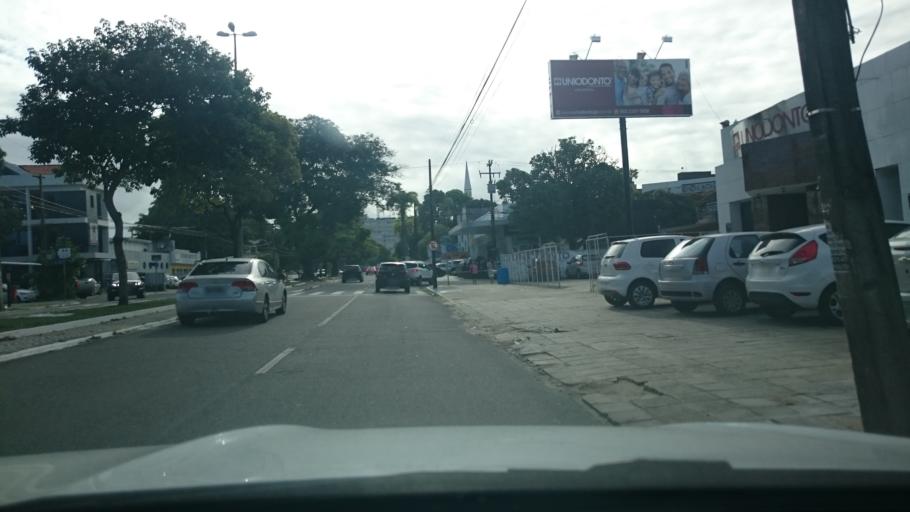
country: BR
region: Paraiba
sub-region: Joao Pessoa
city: Joao Pessoa
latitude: -7.1221
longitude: -34.8727
